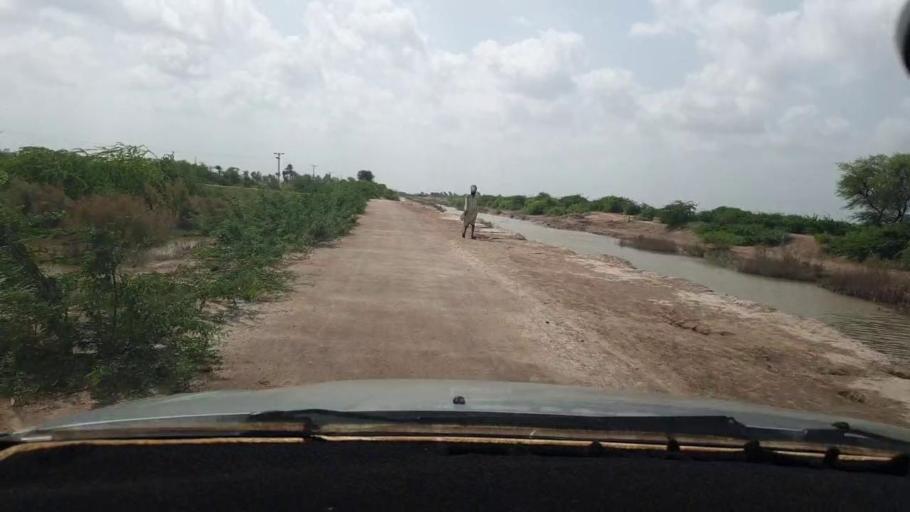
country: PK
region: Sindh
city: Tando Bago
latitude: 24.7219
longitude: 69.1358
